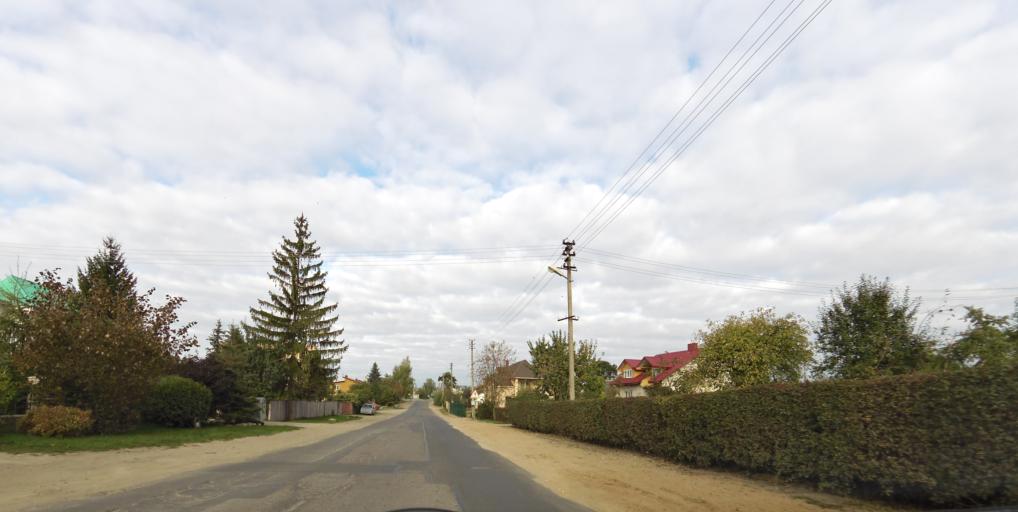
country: LT
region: Vilnius County
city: Pilaite
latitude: 54.7254
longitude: 25.1848
